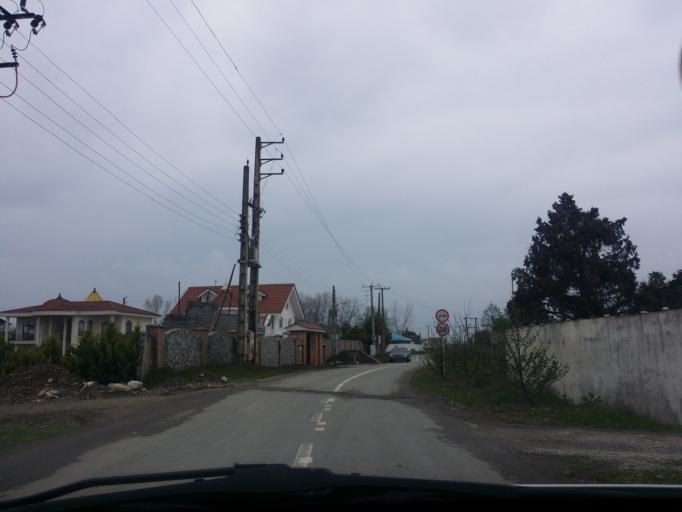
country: IR
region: Mazandaran
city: Chalus
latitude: 36.6816
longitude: 51.3794
